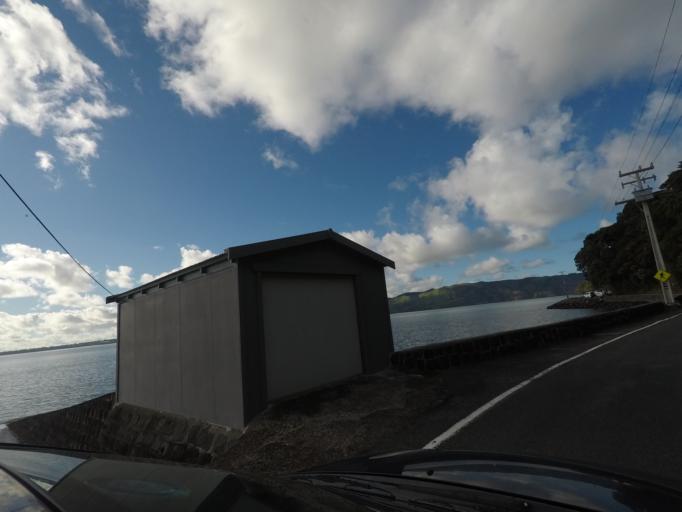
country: NZ
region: Auckland
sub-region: Auckland
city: Titirangi
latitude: -37.0094
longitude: 174.5630
